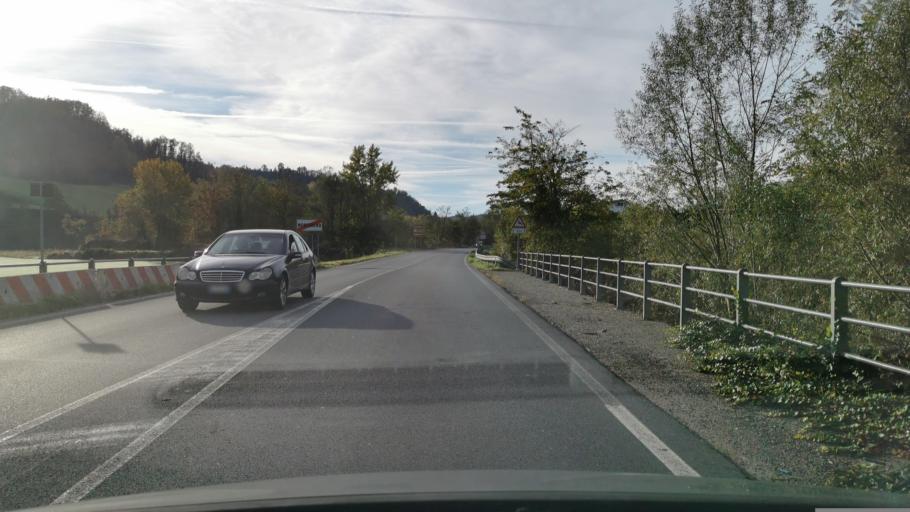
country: IT
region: Piedmont
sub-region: Provincia di Cuneo
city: Monchiero Borgonuovo
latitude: 44.5620
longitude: 7.9226
